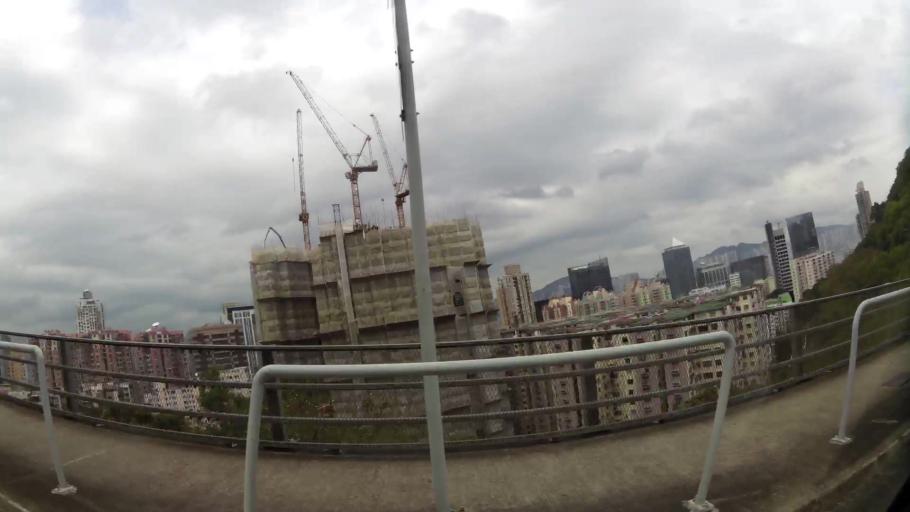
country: HK
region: Wanchai
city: Wan Chai
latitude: 22.2886
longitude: 114.2034
